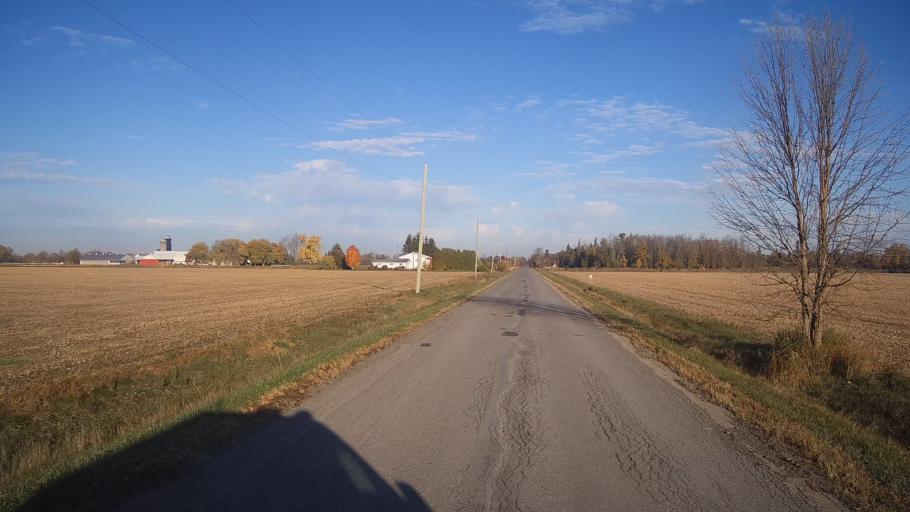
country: CA
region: Ontario
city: Arnprior
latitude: 45.3574
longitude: -76.3080
